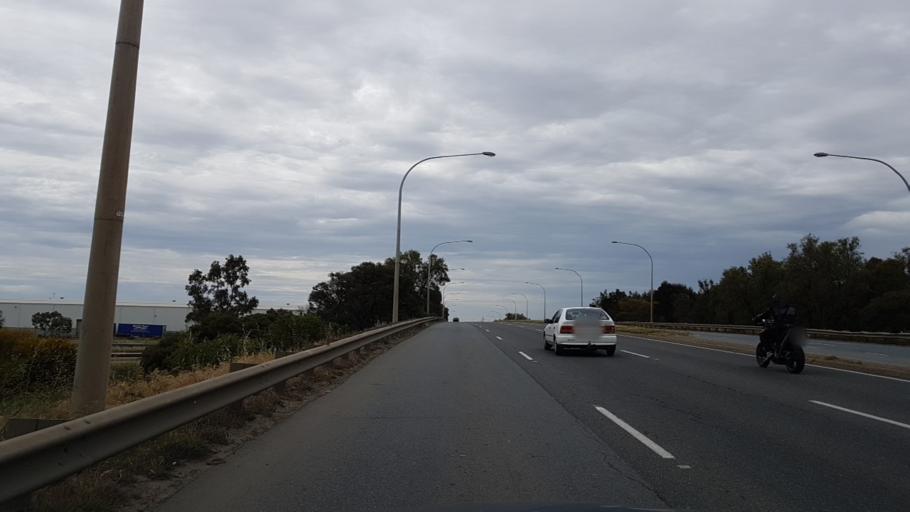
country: AU
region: South Australia
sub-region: Port Adelaide Enfield
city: Enfield
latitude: -34.8214
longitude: 138.5980
